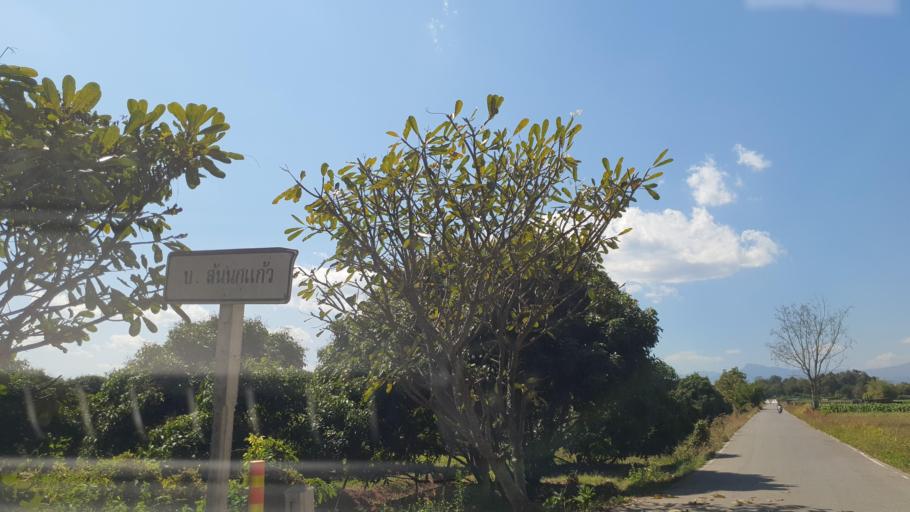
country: TH
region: Chiang Mai
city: Doi Lo
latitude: 18.5327
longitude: 98.8353
